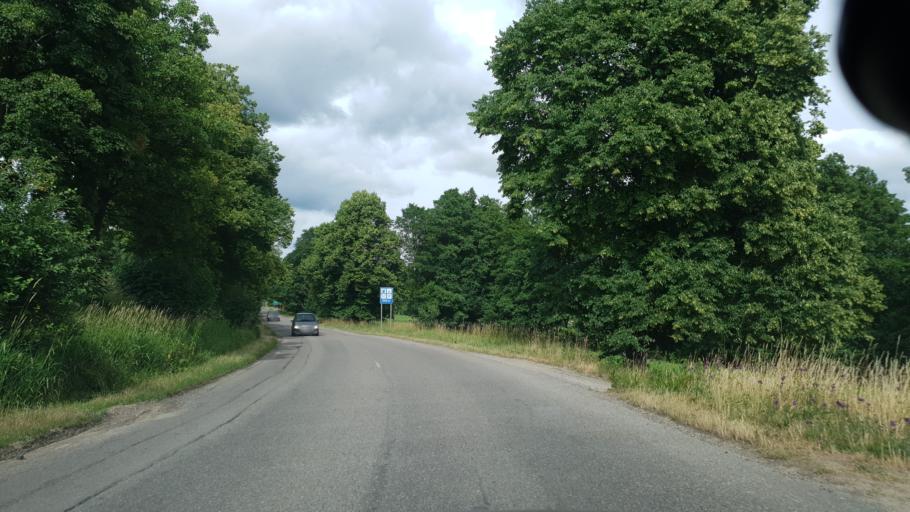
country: PL
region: Pomeranian Voivodeship
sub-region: Powiat kartuski
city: Przodkowo
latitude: 54.3587
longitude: 18.2576
